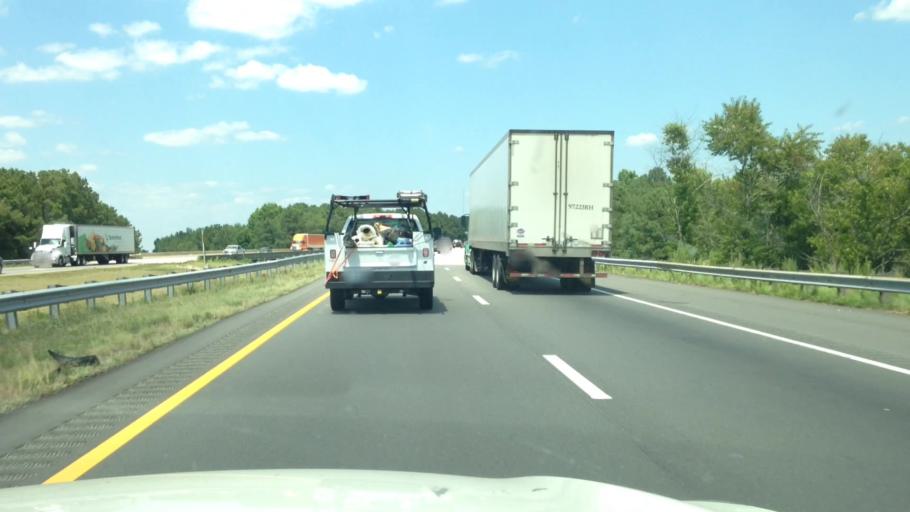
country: US
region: North Carolina
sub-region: Cumberland County
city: Hope Mills
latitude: 34.9301
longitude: -78.9391
